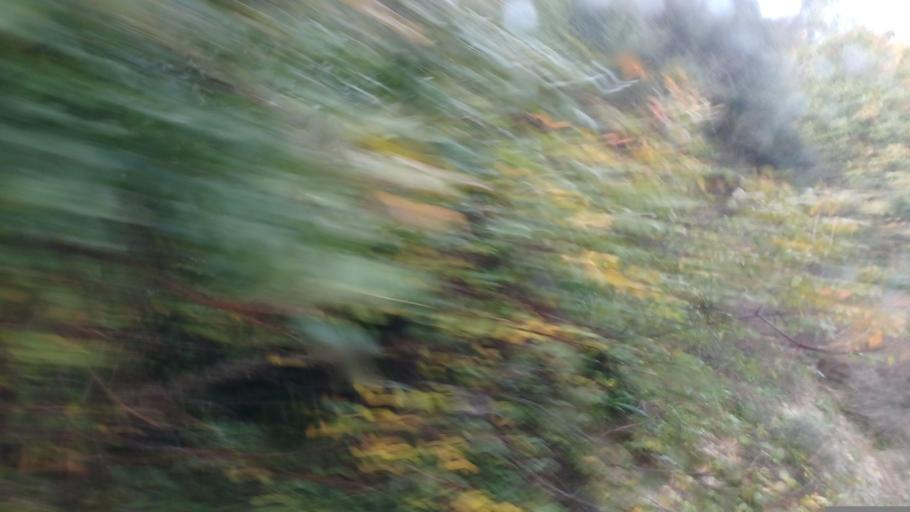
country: CY
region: Pafos
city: Mesogi
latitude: 34.8679
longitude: 32.5337
